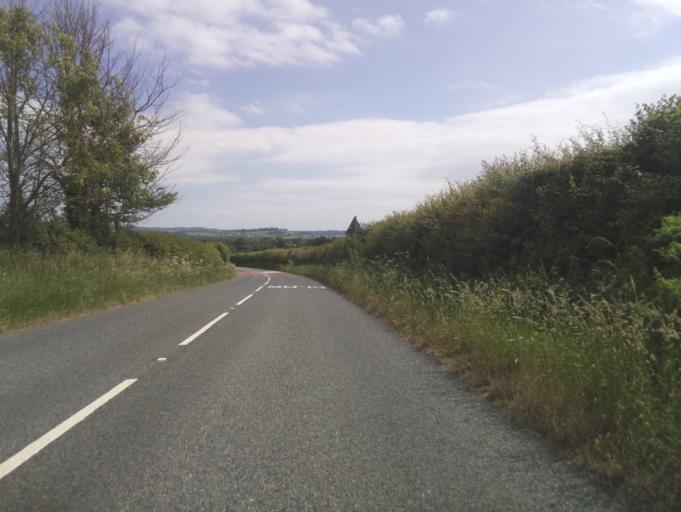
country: GB
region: England
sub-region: Somerset
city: Wincanton
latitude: 51.0344
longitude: -2.4431
